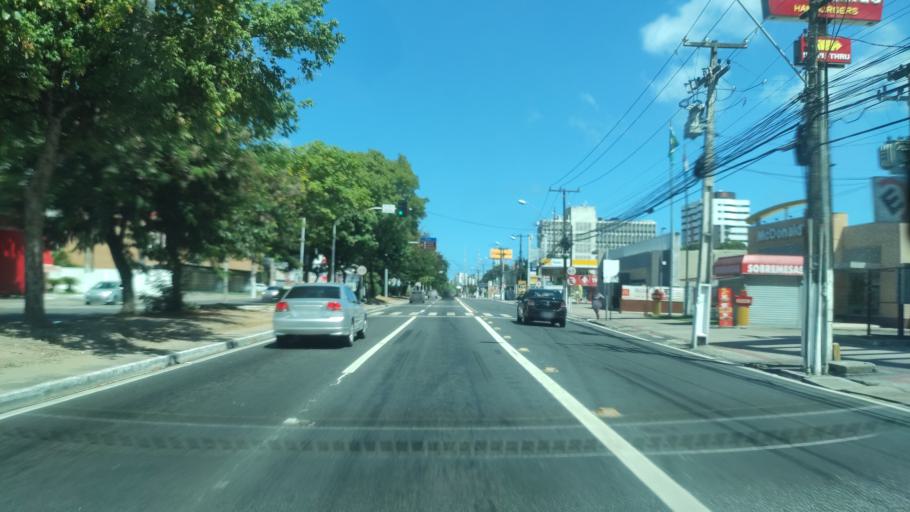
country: BR
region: Alagoas
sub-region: Maceio
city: Maceio
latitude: -9.6450
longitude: -35.7346
